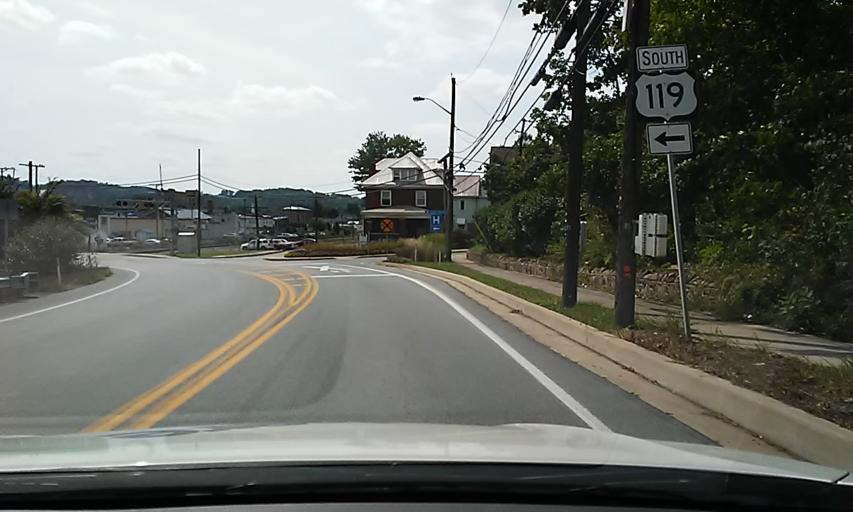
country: US
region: Pennsylvania
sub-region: Jefferson County
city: Punxsutawney
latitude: 40.9480
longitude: -78.9670
